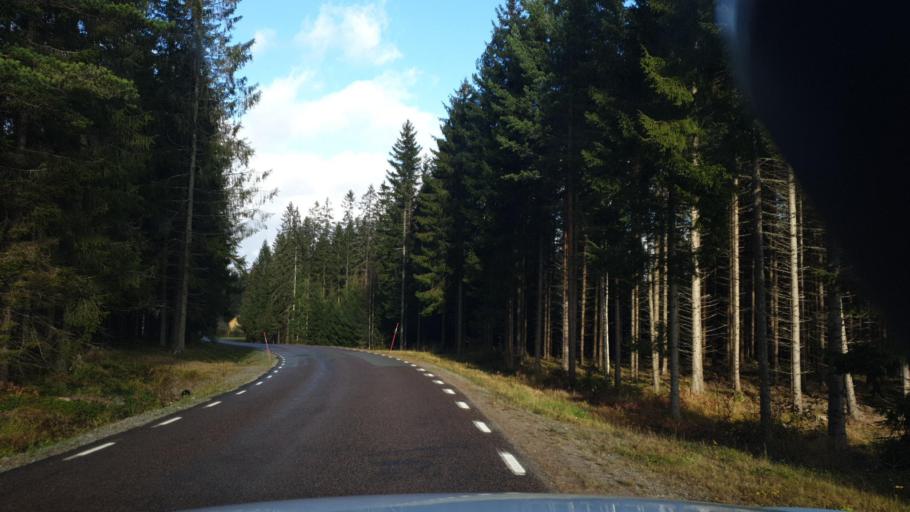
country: SE
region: Vaermland
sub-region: Grums Kommun
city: Grums
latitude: 59.4977
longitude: 12.8777
